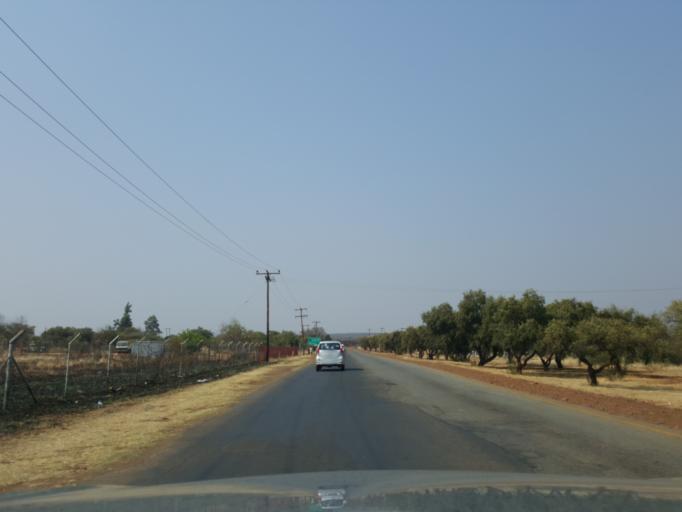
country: ZA
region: North-West
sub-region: Ngaka Modiri Molema District Municipality
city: Zeerust
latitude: -25.5010
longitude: 25.9840
